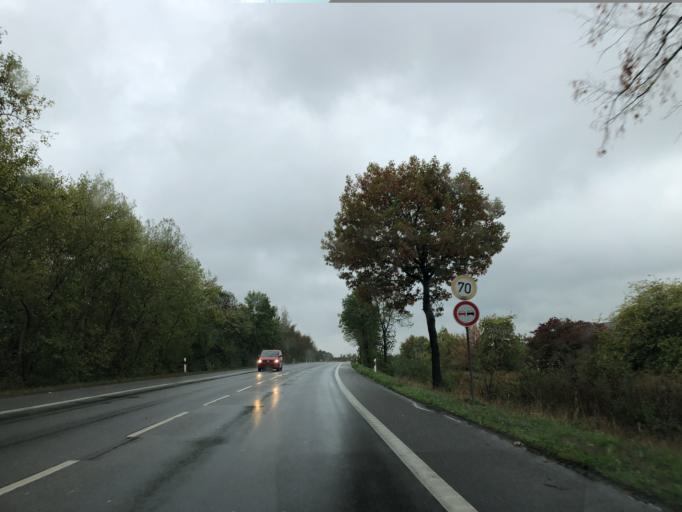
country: DE
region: North Rhine-Westphalia
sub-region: Regierungsbezirk Koln
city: Bedburg
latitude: 51.0216
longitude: 6.5823
